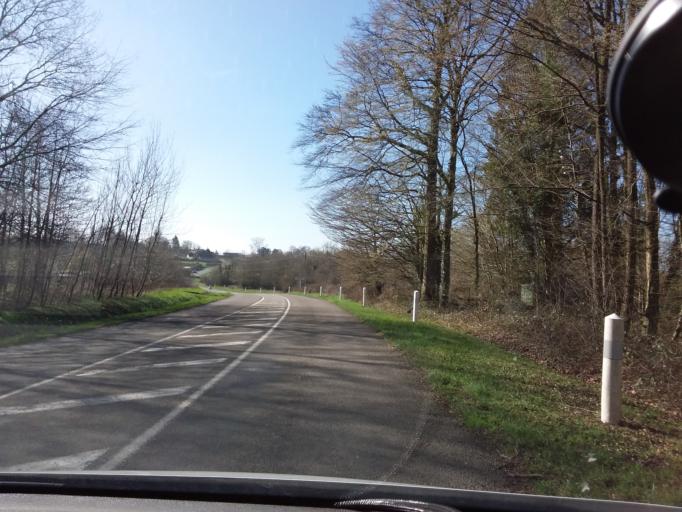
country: FR
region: Nord-Pas-de-Calais
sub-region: Departement du Nord
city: Anor
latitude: 49.9684
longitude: 4.0814
